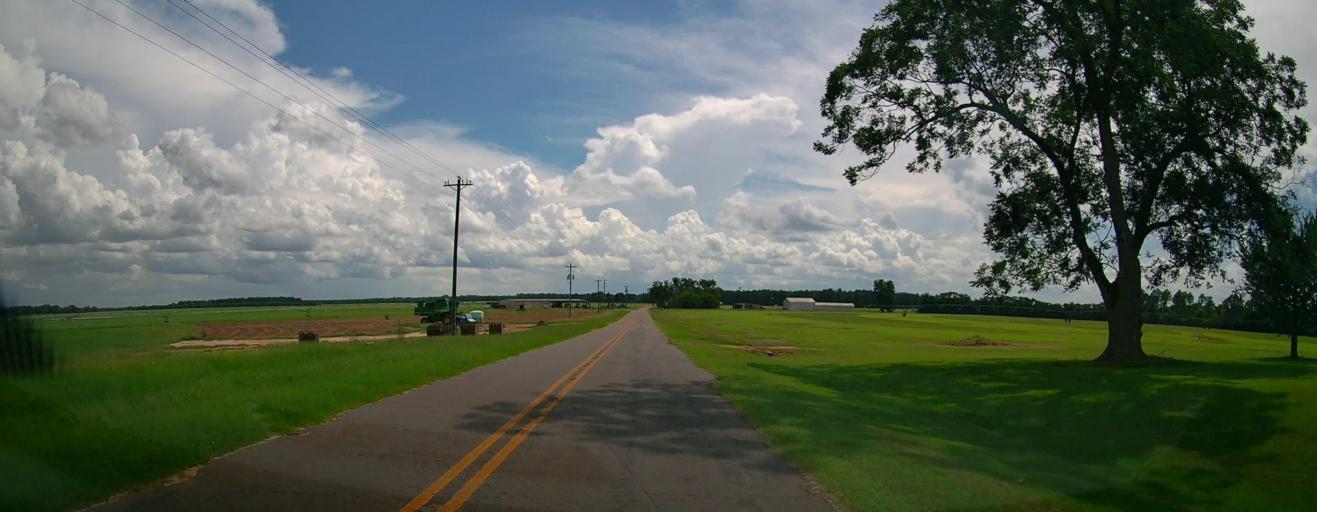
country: US
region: Georgia
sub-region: Macon County
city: Marshallville
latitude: 32.4371
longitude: -84.0006
